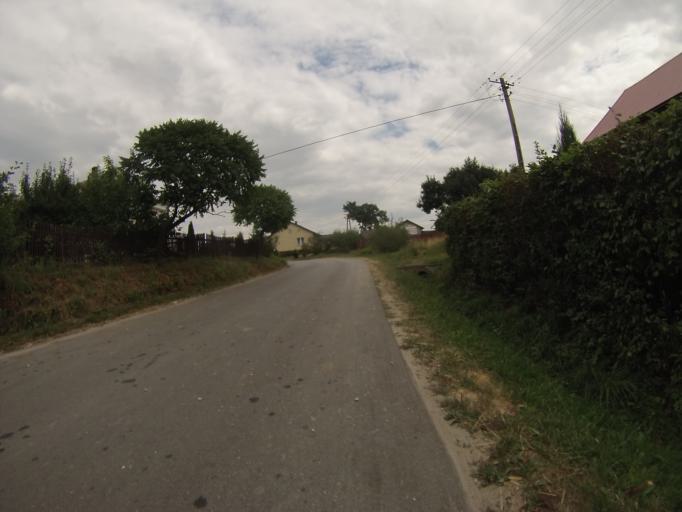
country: PL
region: Swietokrzyskie
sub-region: Powiat staszowski
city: Bogoria
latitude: 50.6856
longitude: 21.2033
